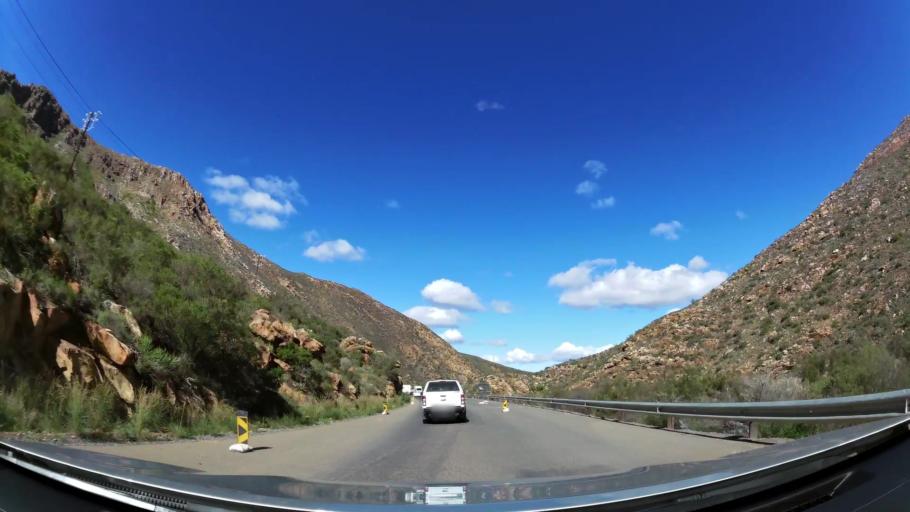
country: ZA
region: Western Cape
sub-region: Cape Winelands District Municipality
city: Ashton
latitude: -33.8169
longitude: 20.0899
